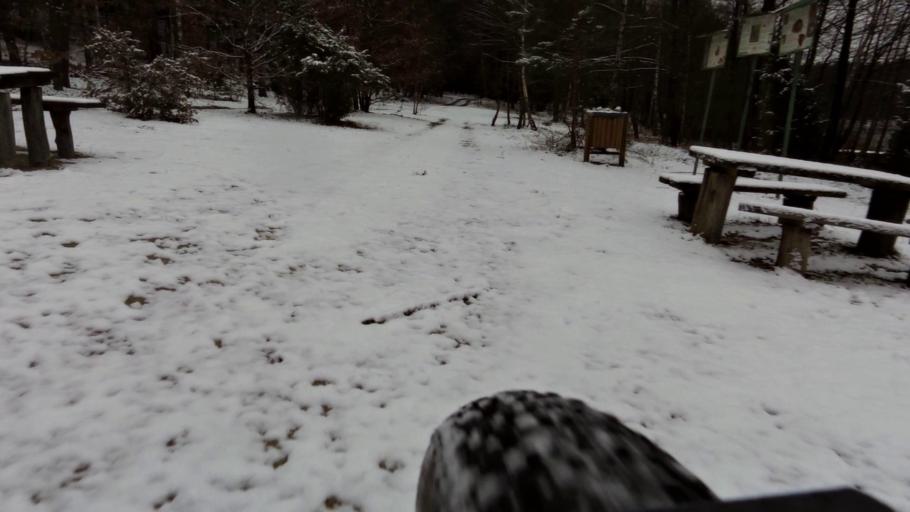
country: PL
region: West Pomeranian Voivodeship
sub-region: Powiat walecki
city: Miroslawiec
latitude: 53.3745
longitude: 16.1629
